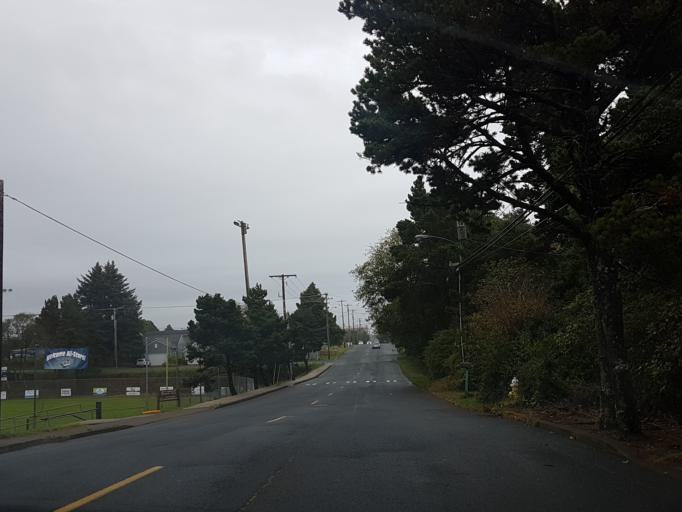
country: US
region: Oregon
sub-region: Lincoln County
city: Newport
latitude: 44.6432
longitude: -124.0556
